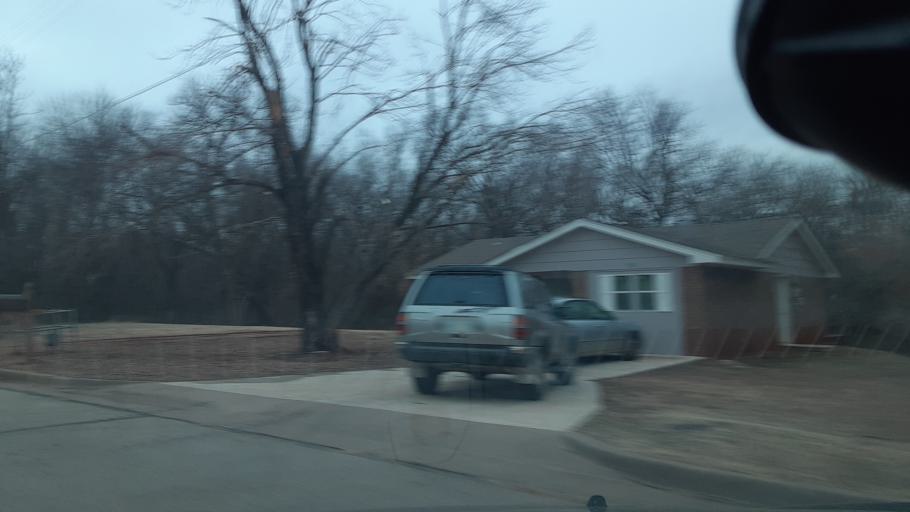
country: US
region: Oklahoma
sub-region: Logan County
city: Guthrie
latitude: 35.8718
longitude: -97.4176
